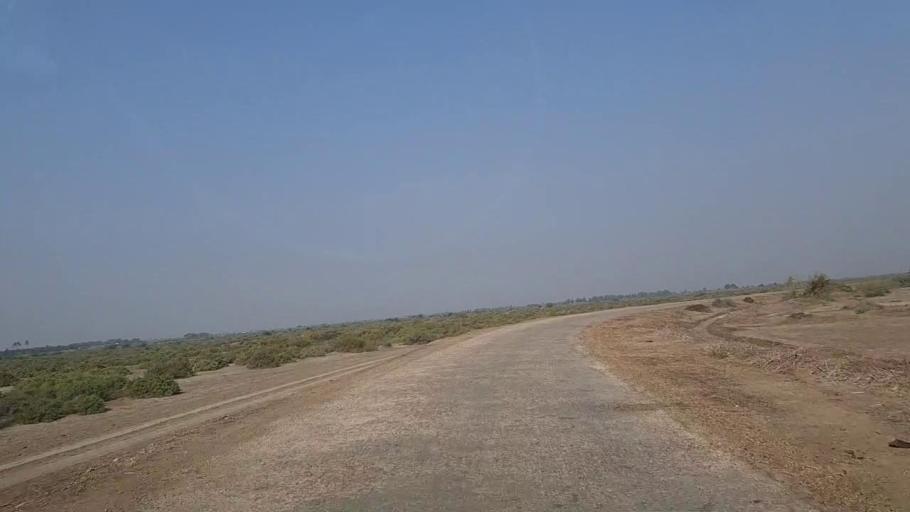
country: PK
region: Sindh
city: Keti Bandar
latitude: 24.2436
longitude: 67.6934
